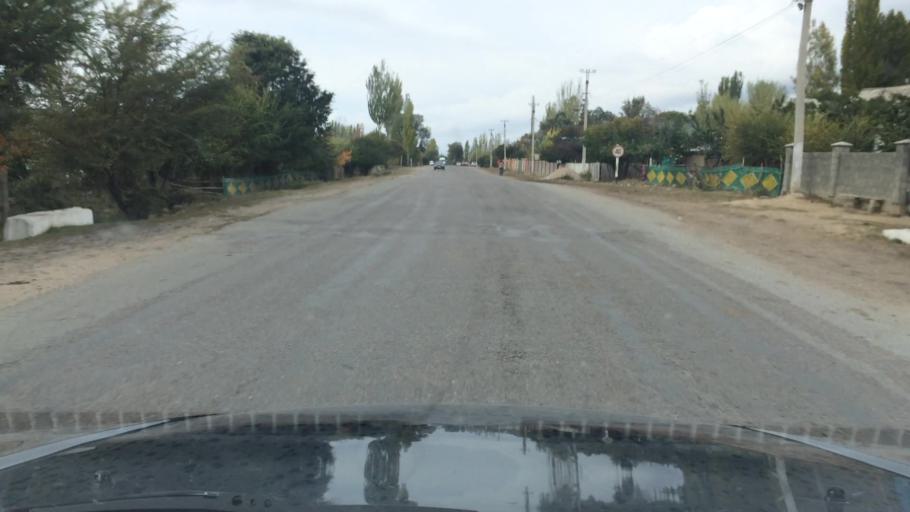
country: KG
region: Ysyk-Koel
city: Pokrovka
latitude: 42.7372
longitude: 77.9432
